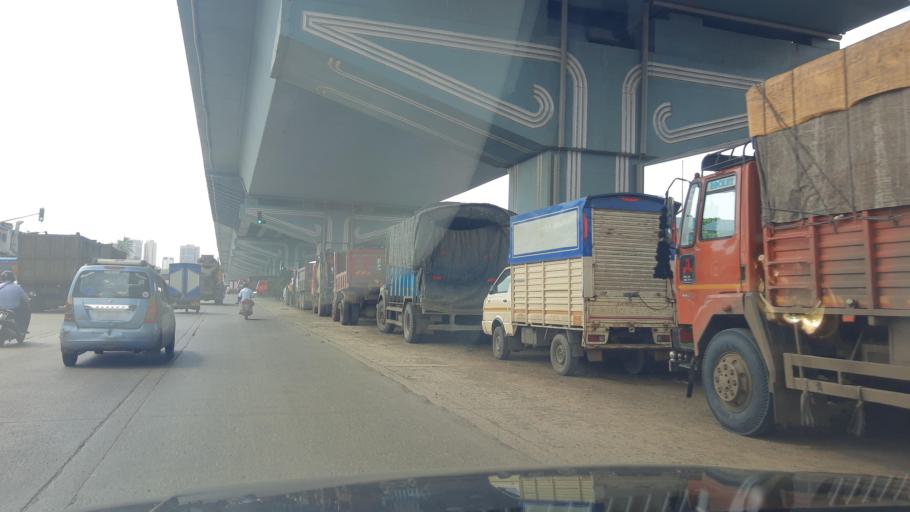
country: IN
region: Maharashtra
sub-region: Mumbai Suburban
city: Mumbai
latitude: 19.0566
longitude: 72.9275
